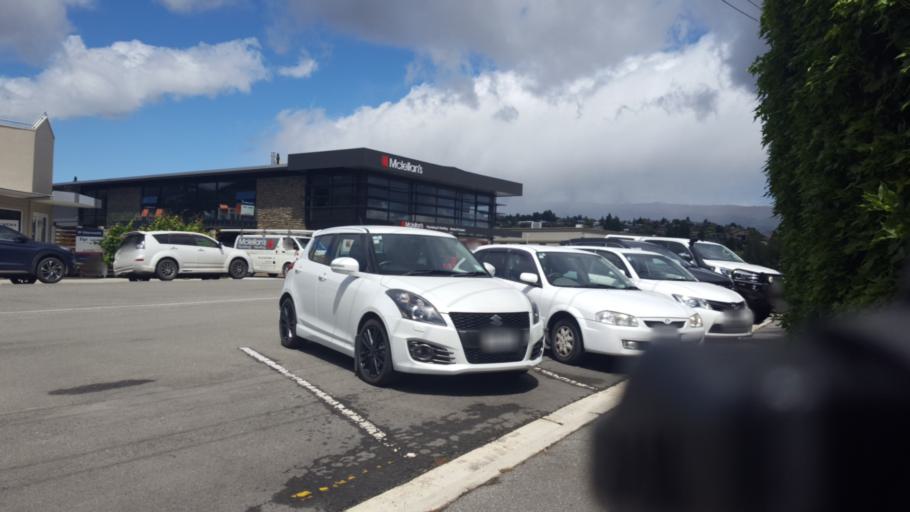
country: NZ
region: Otago
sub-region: Queenstown-Lakes District
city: Wanaka
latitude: -45.2570
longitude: 169.3943
